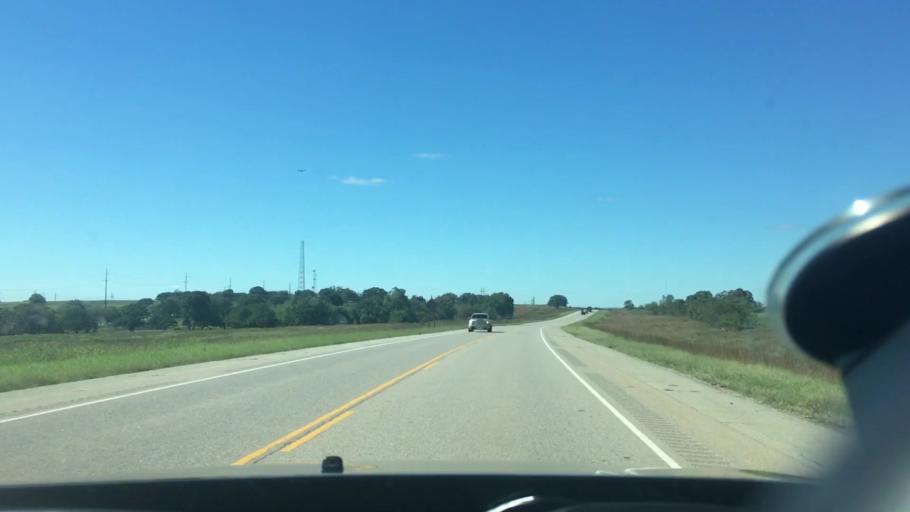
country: US
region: Oklahoma
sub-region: Coal County
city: Coalgate
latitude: 34.6150
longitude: -96.4438
